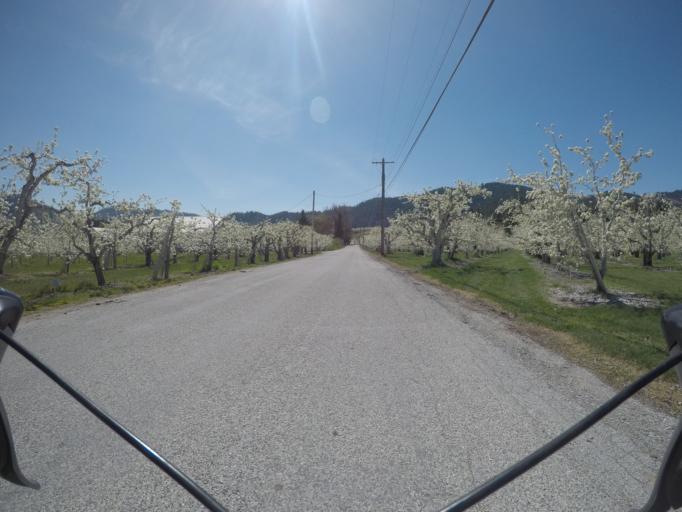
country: US
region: Washington
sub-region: Chelan County
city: Cashmere
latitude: 47.5373
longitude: -120.5611
